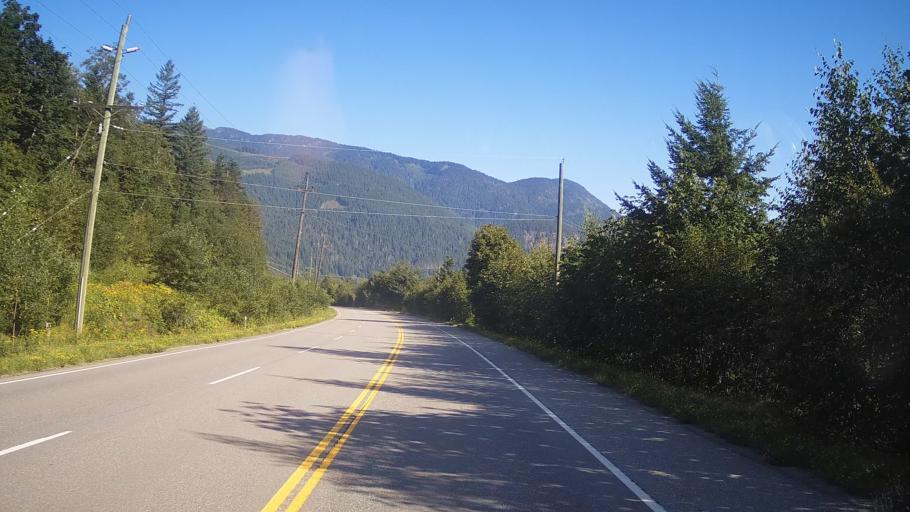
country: CA
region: British Columbia
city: Hope
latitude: 49.5307
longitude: -121.4241
